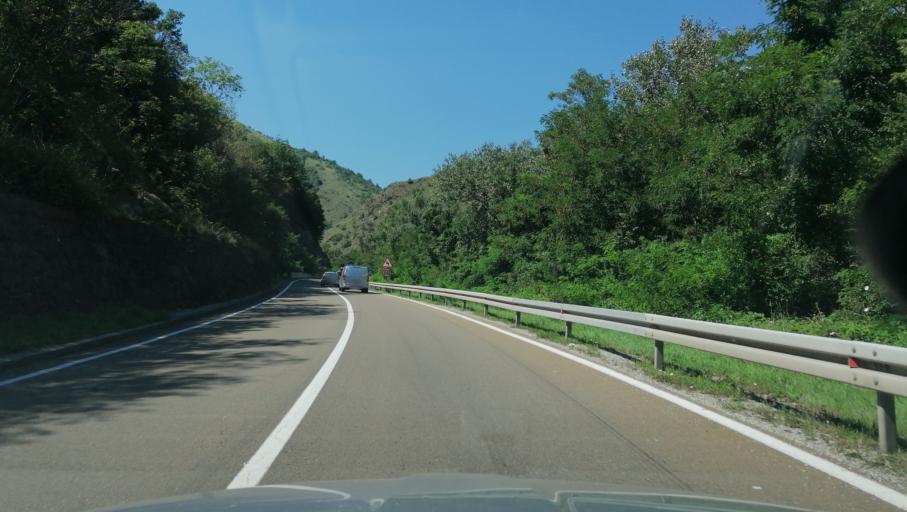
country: RS
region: Central Serbia
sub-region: Raski Okrug
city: Kraljevo
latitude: 43.5805
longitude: 20.5857
